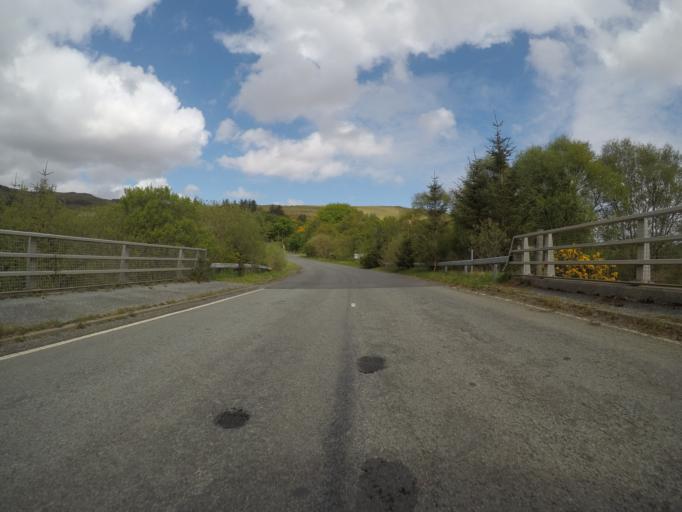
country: GB
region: Scotland
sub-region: Highland
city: Isle of Skye
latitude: 57.2991
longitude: -6.2995
